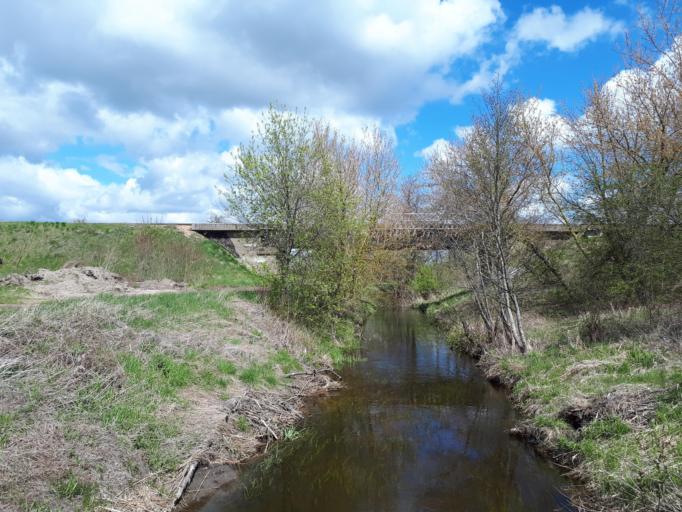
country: LT
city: Simnas
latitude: 54.3864
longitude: 23.7289
